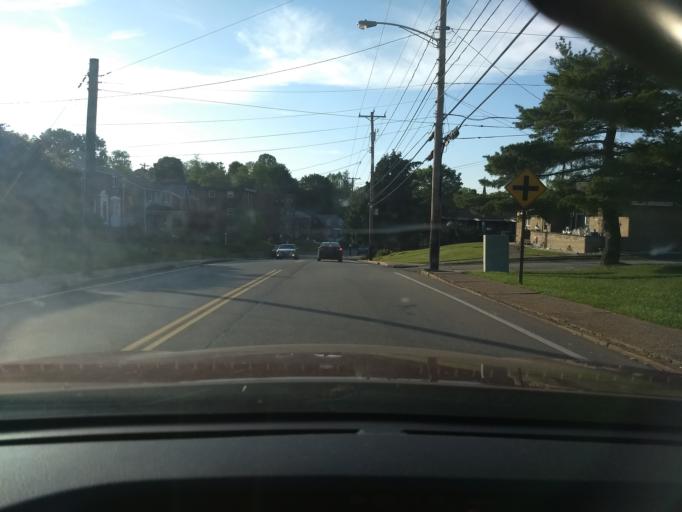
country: US
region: Pennsylvania
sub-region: Allegheny County
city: White Oak
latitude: 40.3492
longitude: -79.8337
